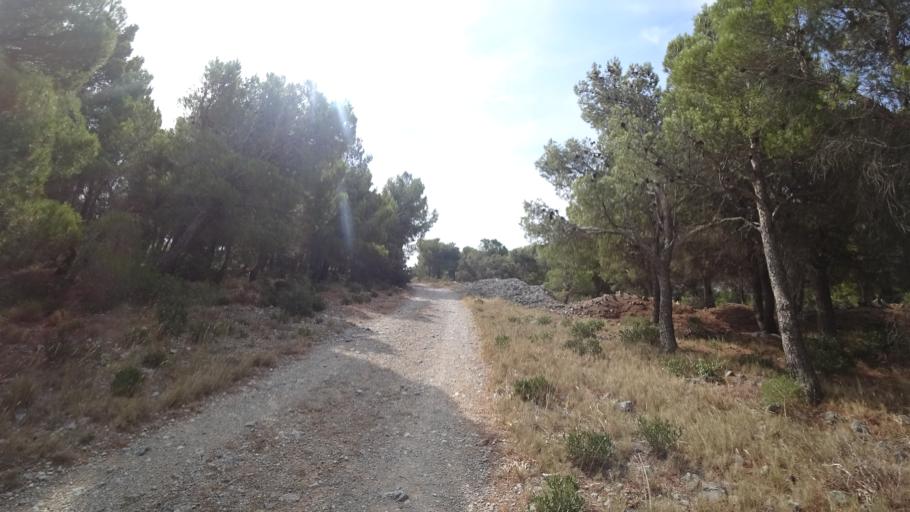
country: FR
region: Languedoc-Roussillon
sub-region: Departement de l'Aude
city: Leucate
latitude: 42.8978
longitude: 3.0210
